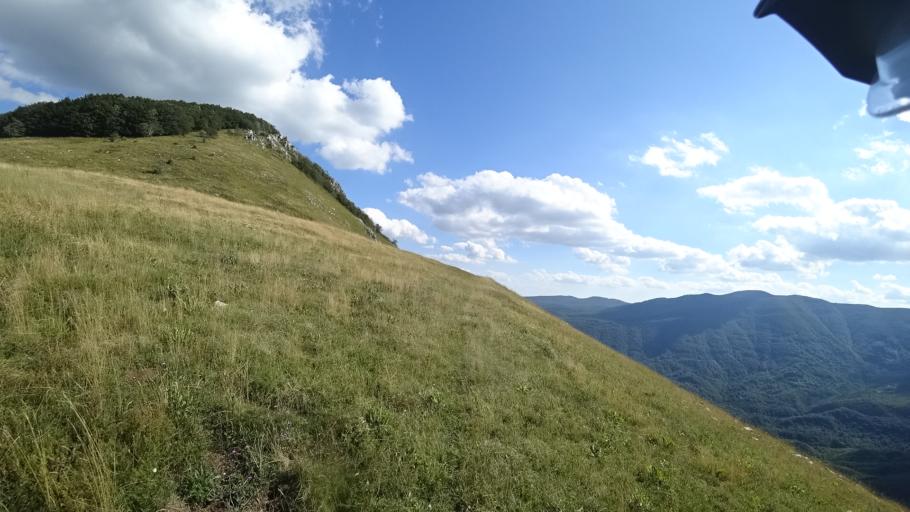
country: HR
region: Zadarska
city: Gracac
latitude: 44.3832
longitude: 16.0462
